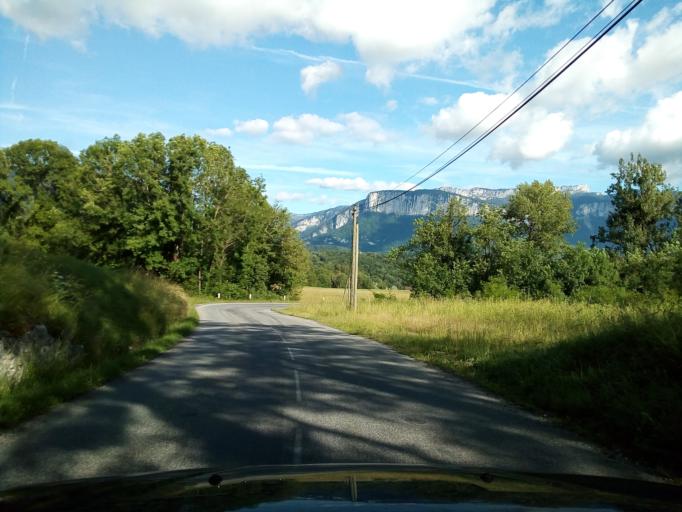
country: FR
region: Rhone-Alpes
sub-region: Departement de la Savoie
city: Les Echelles
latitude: 45.4534
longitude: 5.7458
